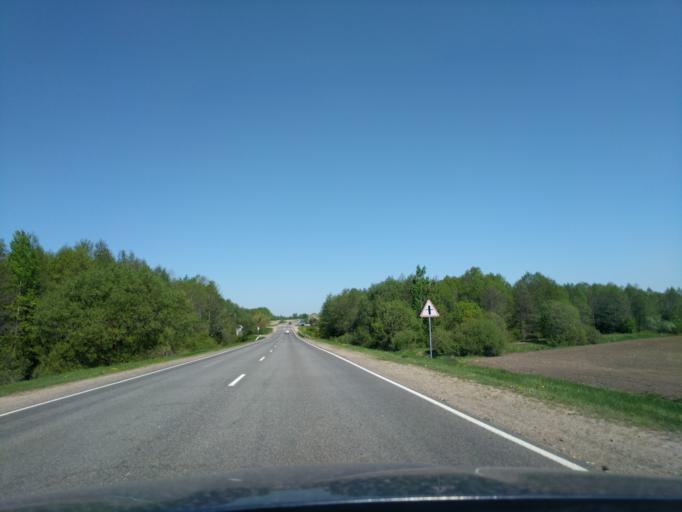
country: BY
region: Minsk
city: Il'ya
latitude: 54.2967
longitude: 27.4806
